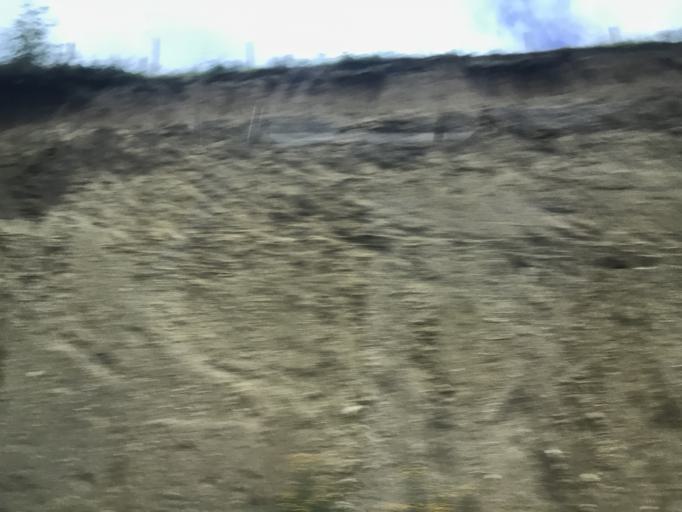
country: GT
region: Chimaltenango
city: El Tejar
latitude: 14.6366
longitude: -90.7877
